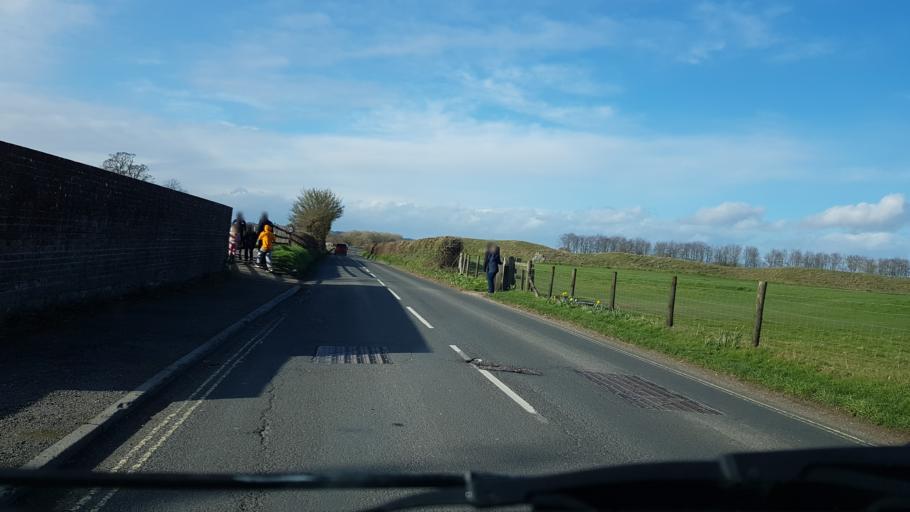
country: GB
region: England
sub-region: Wiltshire
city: Avebury
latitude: 51.4287
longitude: -1.8542
